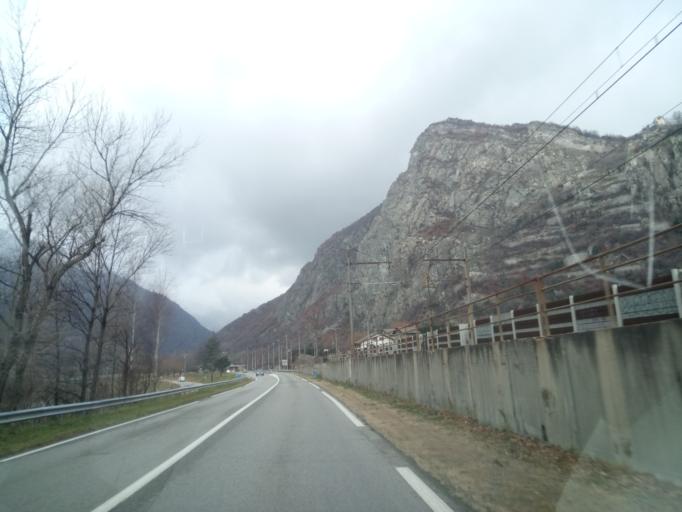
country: FR
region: Rhone-Alpes
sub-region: Departement de la Savoie
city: Saint-Jean-de-Maurienne
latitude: 45.3124
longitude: 6.3398
